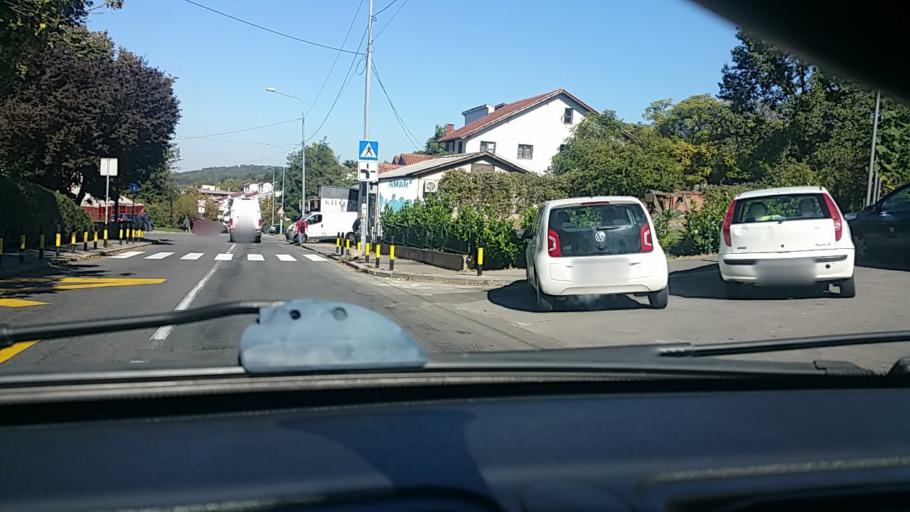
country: RS
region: Central Serbia
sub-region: Belgrade
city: Rakovica
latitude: 44.7477
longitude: 20.4610
